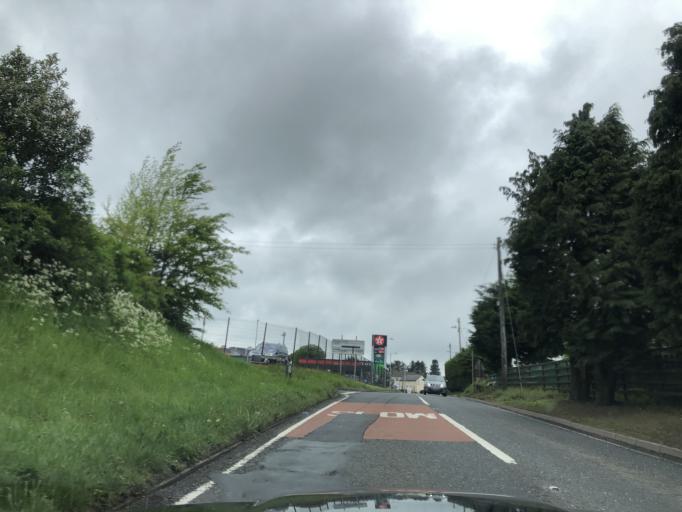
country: GB
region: Northern Ireland
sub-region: Lisburn District
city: Lisburn
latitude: 54.5475
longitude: -6.0749
